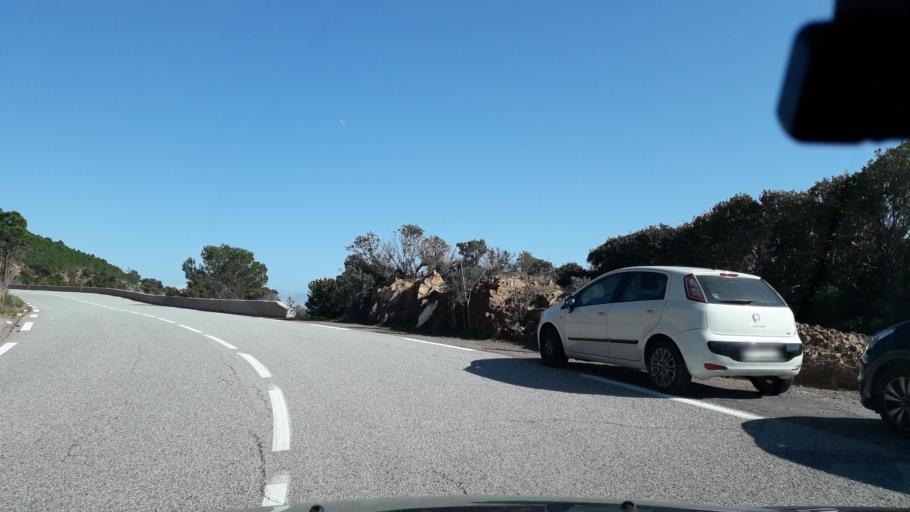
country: FR
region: Provence-Alpes-Cote d'Azur
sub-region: Departement des Alpes-Maritimes
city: Theoule-sur-Mer
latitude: 43.4463
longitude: 6.9077
